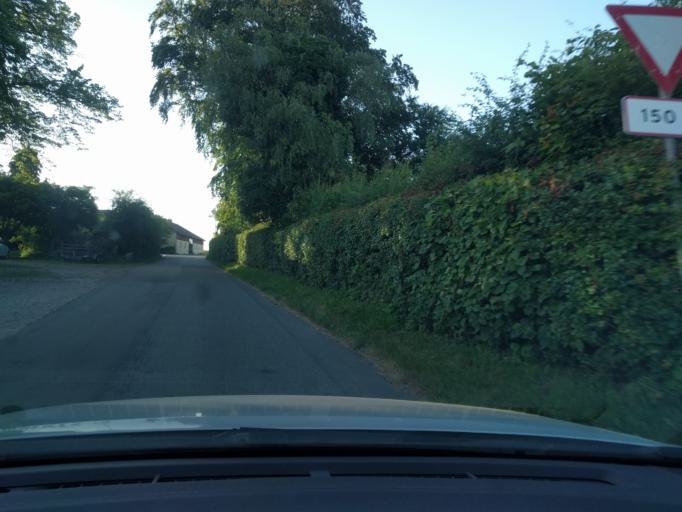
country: DK
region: Zealand
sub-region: Vordingborg Kommune
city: Stege
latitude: 54.9653
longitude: 12.2318
